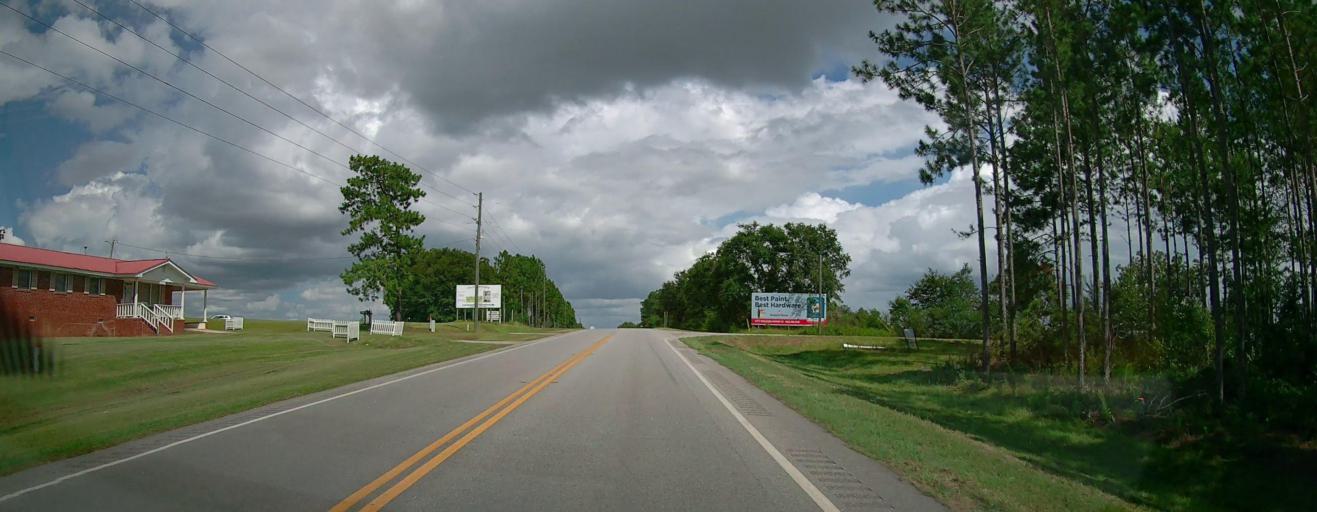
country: US
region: Georgia
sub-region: Coffee County
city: Broxton
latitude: 31.5791
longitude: -83.0568
